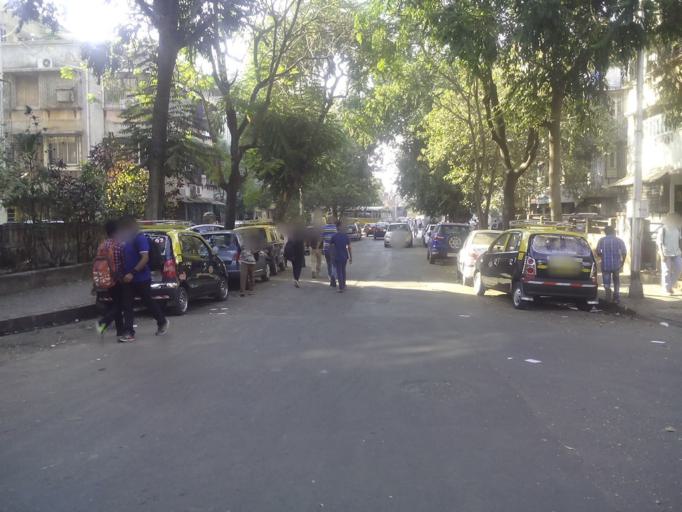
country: IN
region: Maharashtra
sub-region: Mumbai Suburban
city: Mumbai
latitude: 19.0400
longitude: 72.8609
